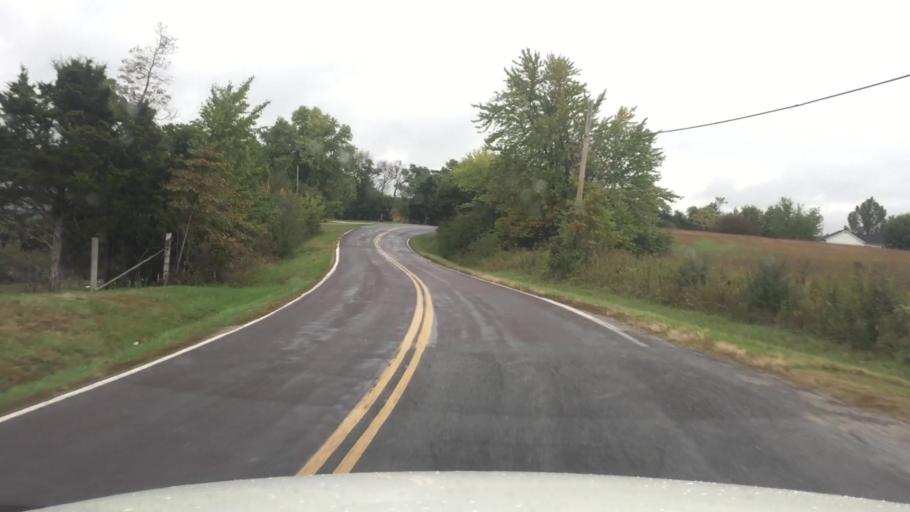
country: US
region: Missouri
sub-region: Boone County
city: Ashland
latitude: 38.7176
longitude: -92.2781
